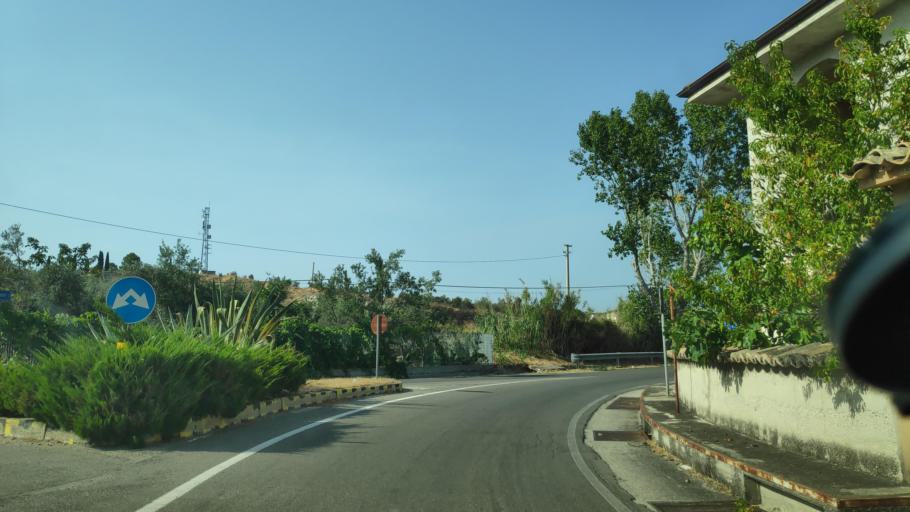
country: IT
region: Calabria
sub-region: Provincia di Catanzaro
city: Isca Marina
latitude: 38.6071
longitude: 16.5535
